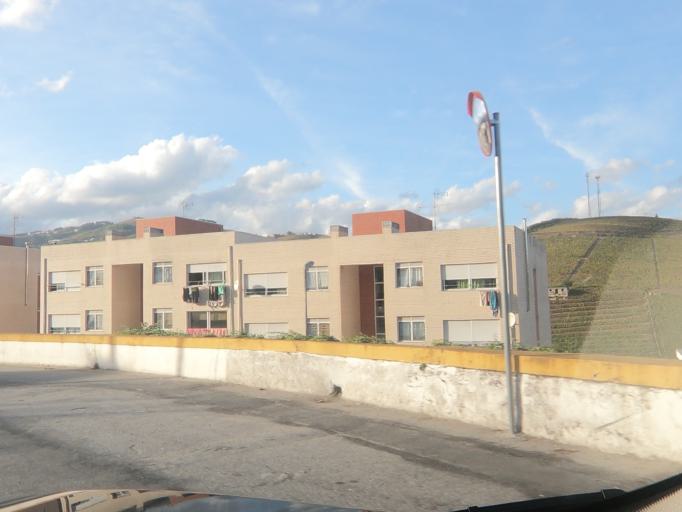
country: PT
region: Vila Real
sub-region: Santa Marta de Penaguiao
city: Santa Marta de Penaguiao
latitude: 41.2083
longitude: -7.7803
